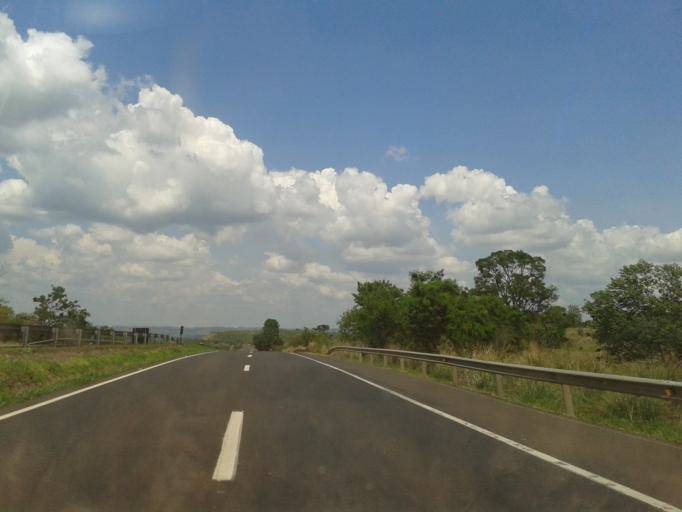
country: BR
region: Minas Gerais
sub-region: Araguari
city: Araguari
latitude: -18.7120
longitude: -48.1960
